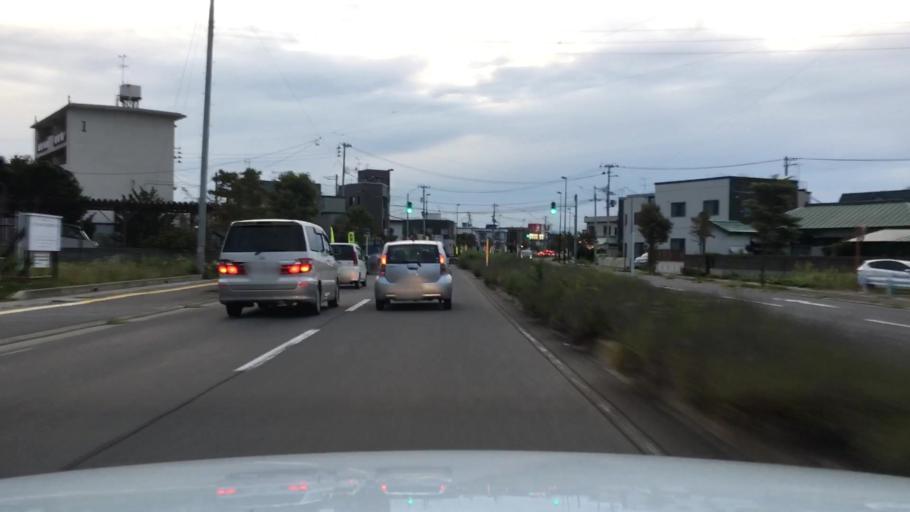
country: JP
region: Aomori
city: Hirosaki
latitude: 40.5917
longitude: 140.4769
